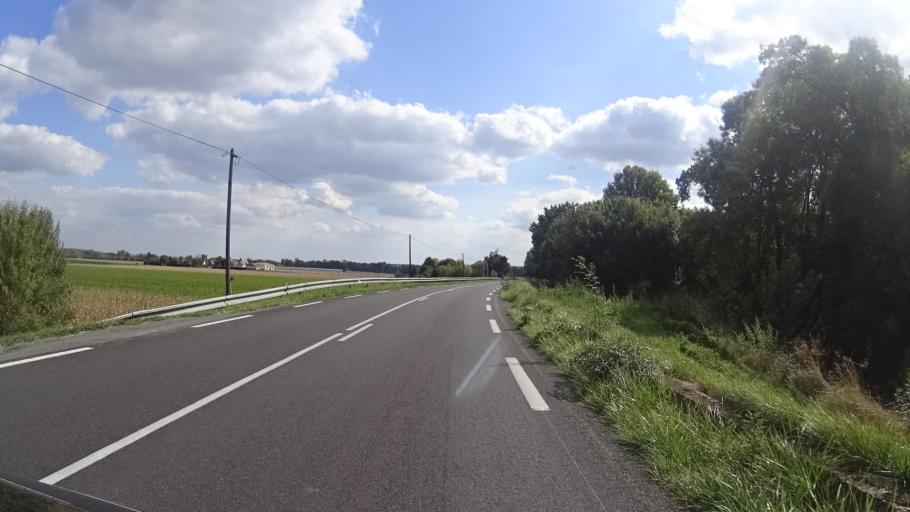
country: FR
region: Pays de la Loire
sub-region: Departement de Maine-et-Loire
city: La Menitre
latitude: 47.3711
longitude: -0.2552
